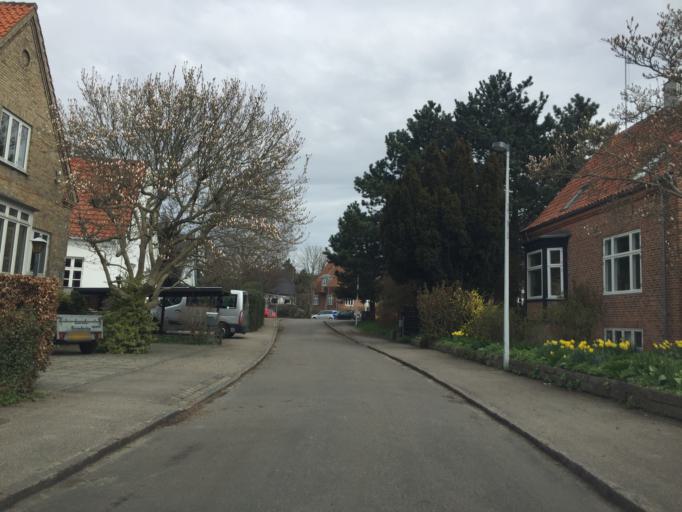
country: DK
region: Capital Region
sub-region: Kobenhavn
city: Vanlose
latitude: 55.7099
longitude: 12.5067
